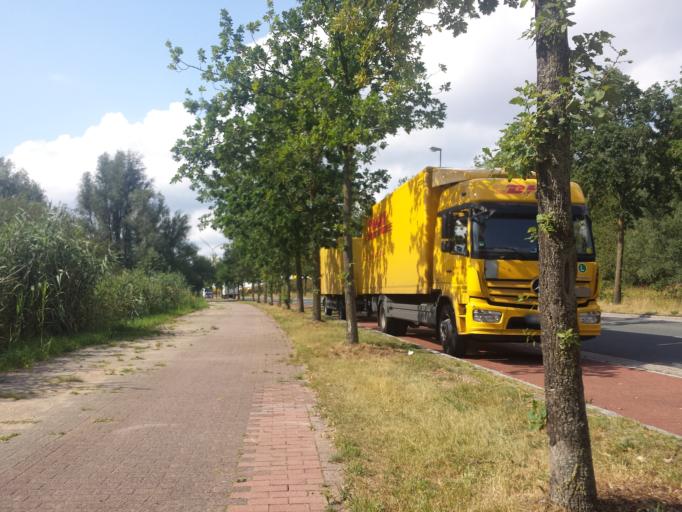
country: DE
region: Lower Saxony
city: Stuhr
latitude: 53.0958
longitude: 8.7093
